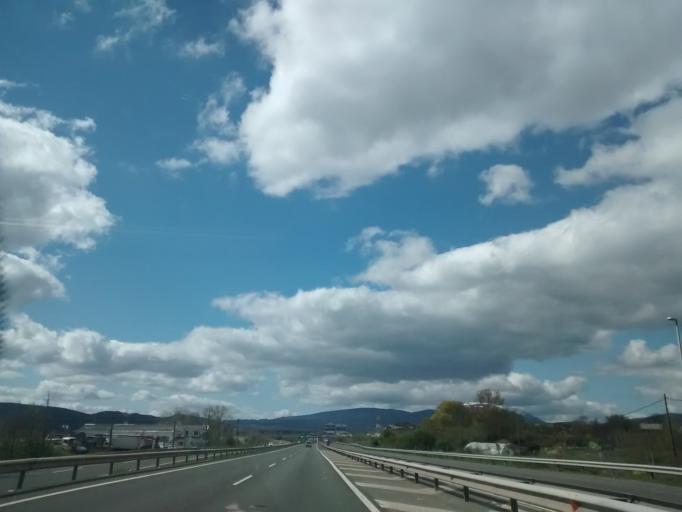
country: ES
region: Basque Country
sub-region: Provincia de Alava
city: Gasteiz / Vitoria
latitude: 42.8965
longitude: -2.7040
